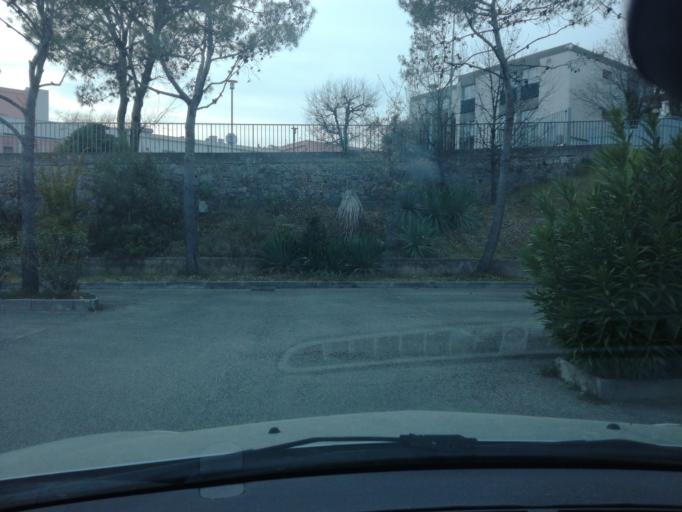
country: FR
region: Provence-Alpes-Cote d'Azur
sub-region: Departement des Alpes-Maritimes
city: Grasse
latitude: 43.6377
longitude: 6.9113
